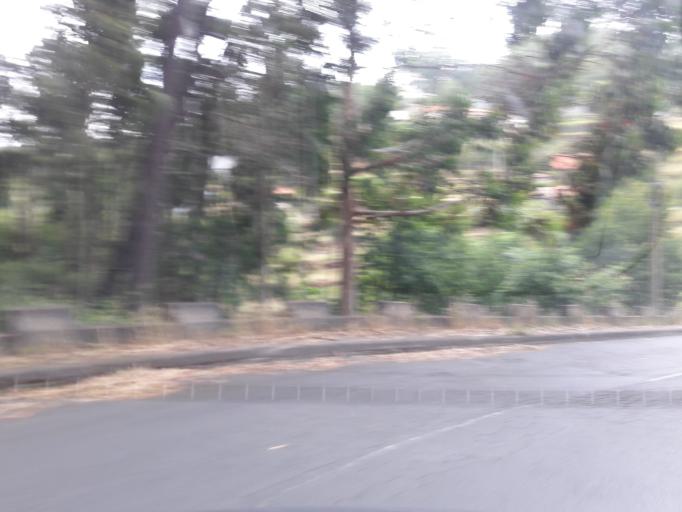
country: PT
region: Madeira
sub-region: Santa Cruz
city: Camacha
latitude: 32.6914
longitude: -16.8688
